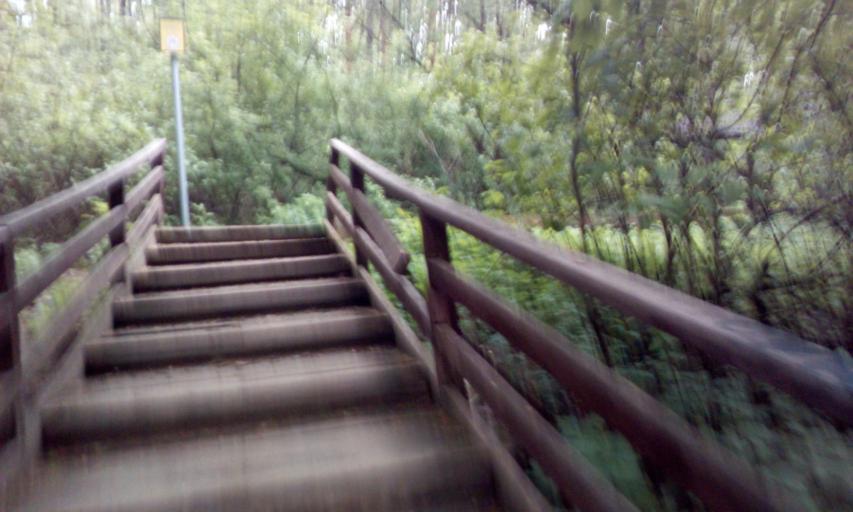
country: RU
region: Moskovskaya
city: Vostryakovo
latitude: 55.6509
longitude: 37.4580
